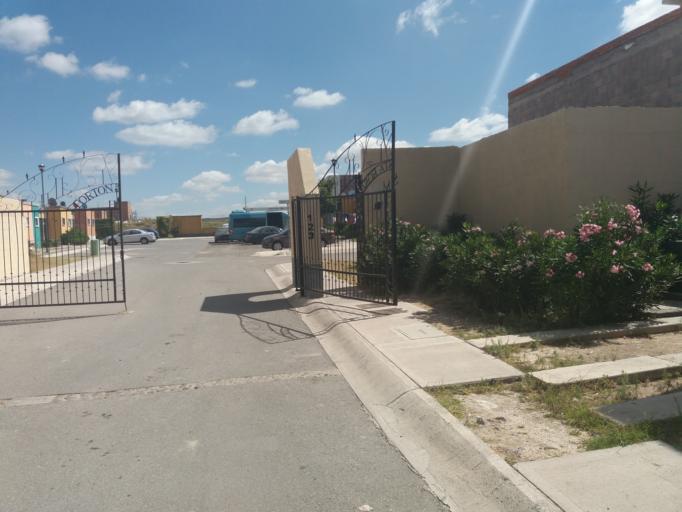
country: MX
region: Aguascalientes
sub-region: Aguascalientes
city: San Sebastian [Fraccionamiento]
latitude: 21.7933
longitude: -102.2754
